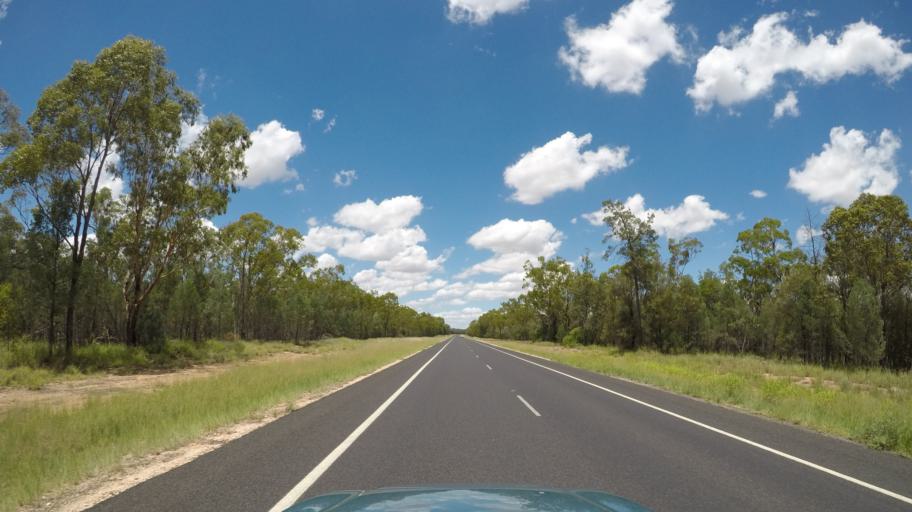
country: AU
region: Queensland
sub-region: Goondiwindi
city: Goondiwindi
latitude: -28.1000
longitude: 150.7247
